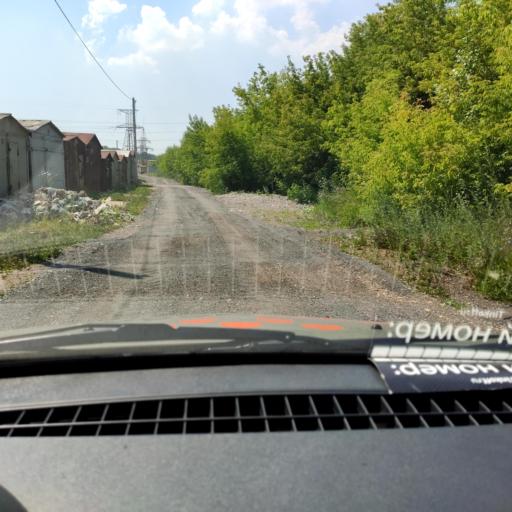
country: RU
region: Bashkortostan
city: Ufa
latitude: 54.7934
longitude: 56.0968
